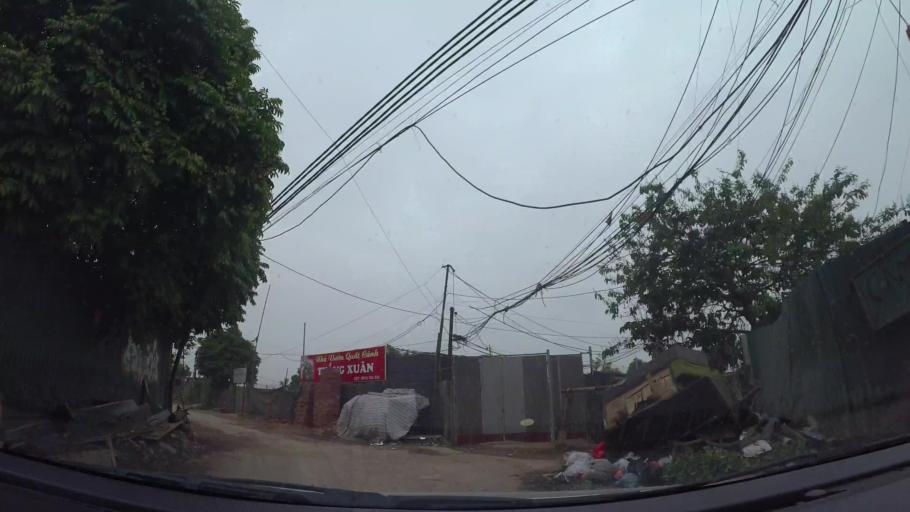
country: VN
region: Ha Noi
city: Tay Ho
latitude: 21.0610
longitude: 105.8394
